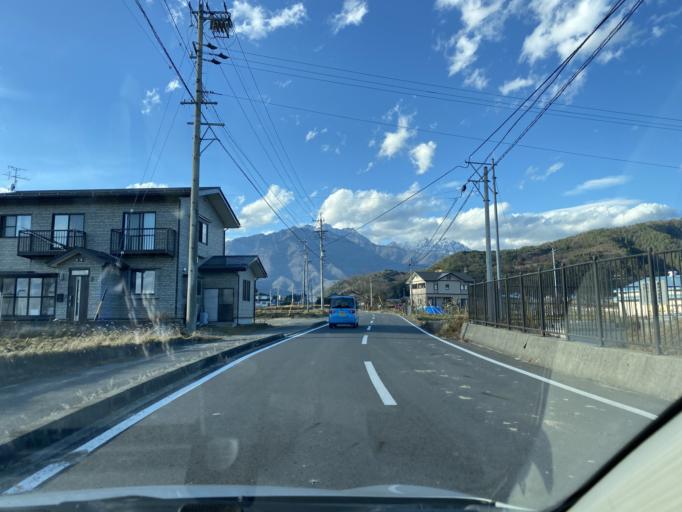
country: JP
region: Nagano
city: Omachi
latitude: 36.5228
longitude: 137.8331
